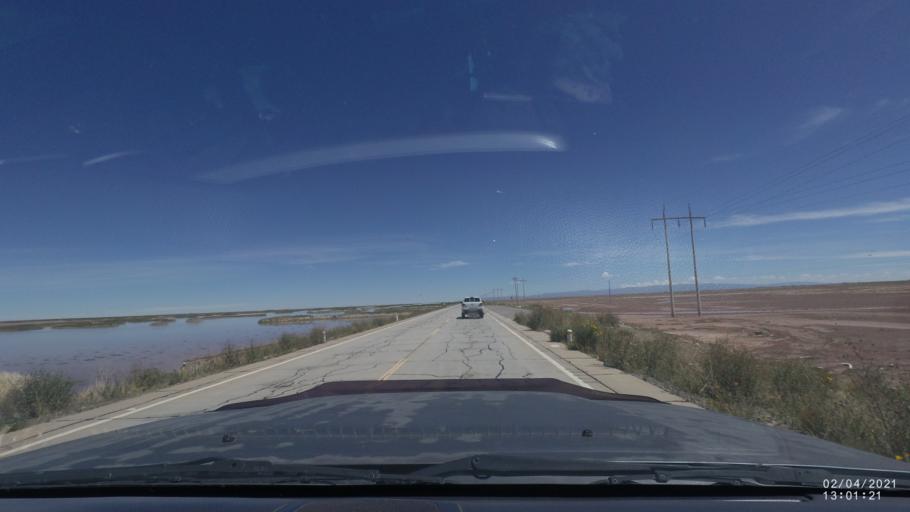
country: BO
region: Oruro
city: Oruro
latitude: -18.0413
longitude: -67.1682
